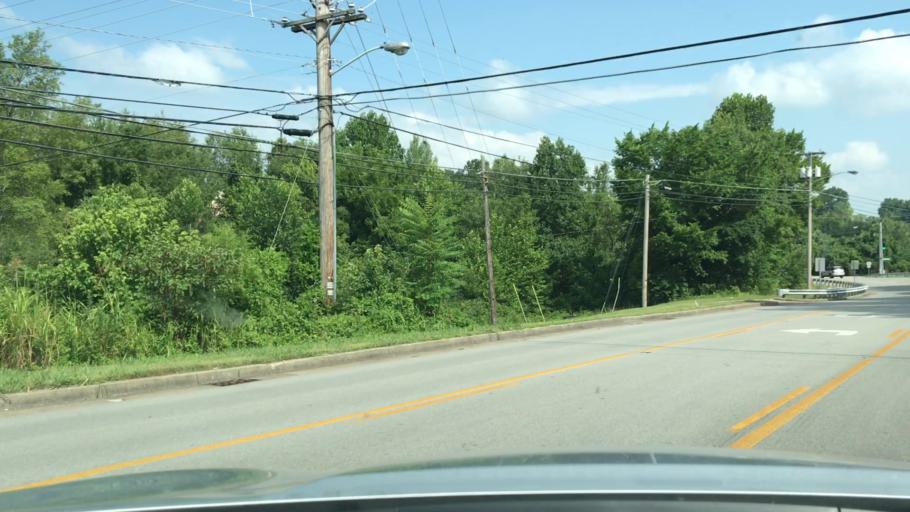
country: US
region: Kentucky
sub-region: Barren County
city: Glasgow
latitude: 37.0167
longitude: -85.9065
